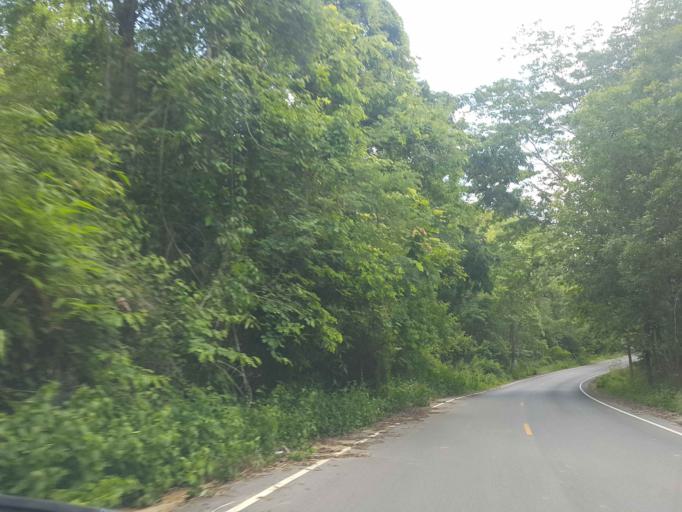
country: TH
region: Nan
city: Wiang Sa
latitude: 18.5297
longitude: 100.5547
